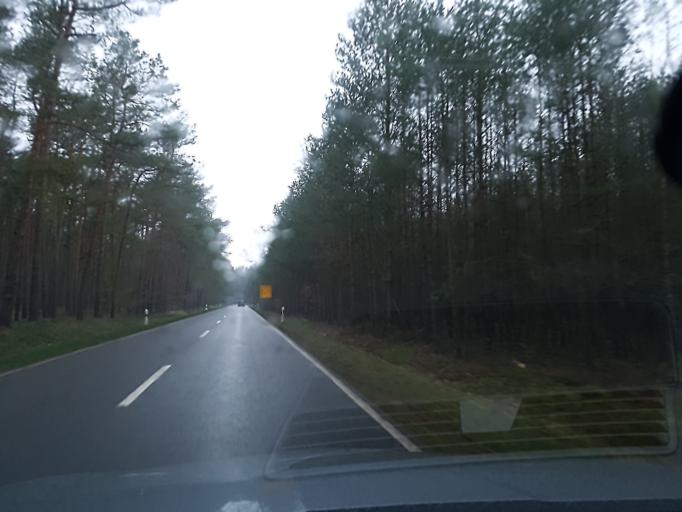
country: DE
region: Brandenburg
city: Schonborn
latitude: 51.6595
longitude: 13.5055
